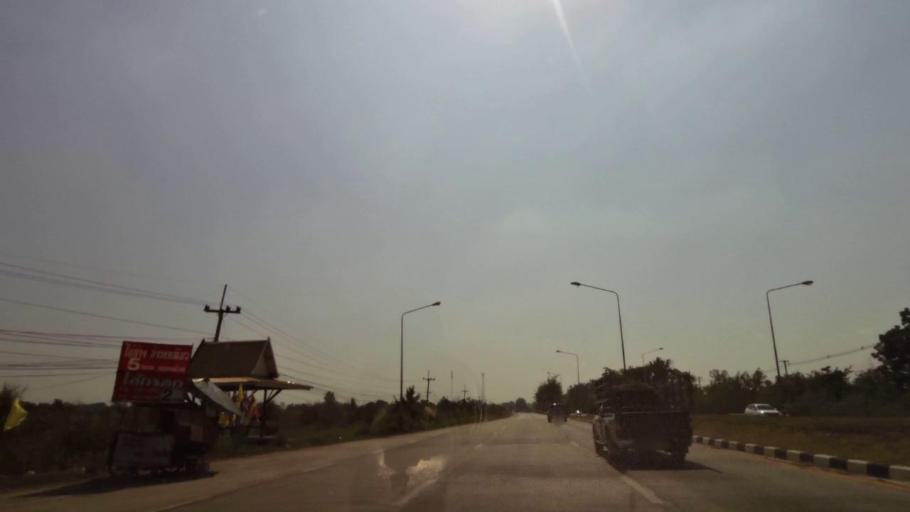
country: TH
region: Phichit
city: Wachira Barami
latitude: 16.3532
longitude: 100.1289
